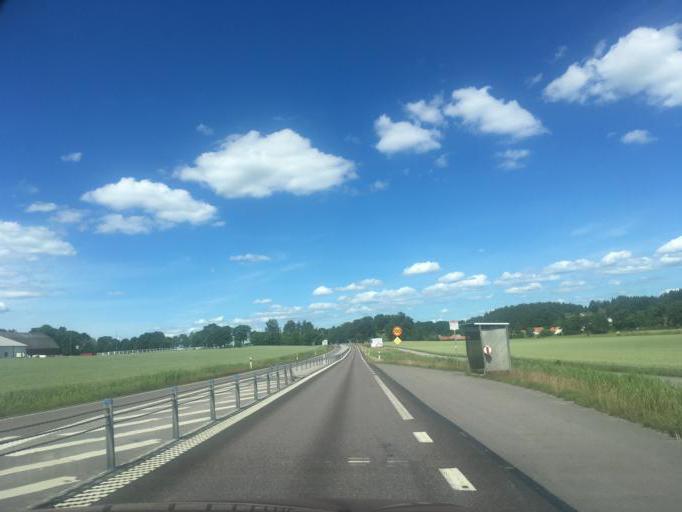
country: SE
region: OEstergoetland
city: Lindo
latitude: 58.5428
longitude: 16.2708
